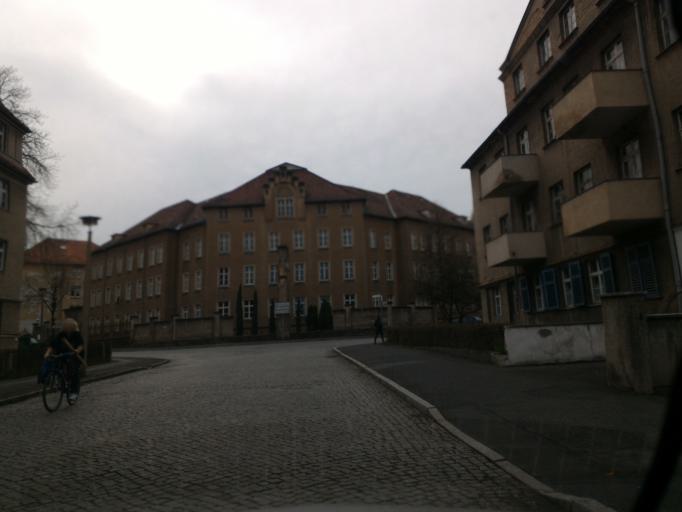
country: DE
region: Saxony
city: Zittau
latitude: 50.8843
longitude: 14.8079
